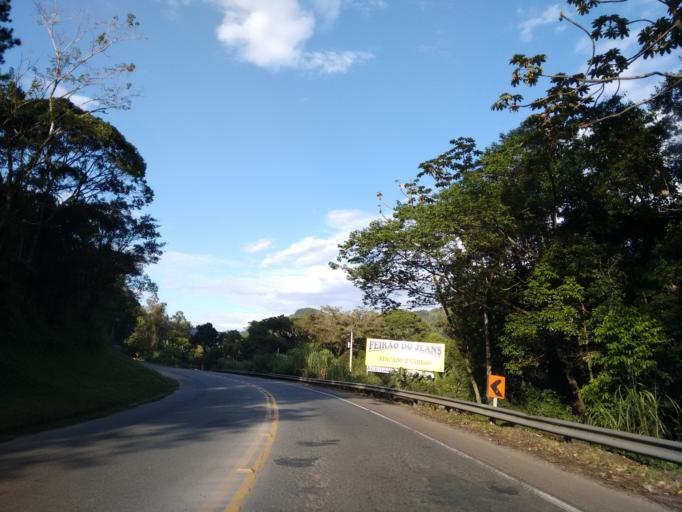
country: BR
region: Santa Catarina
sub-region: Ibirama
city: Ibirama
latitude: -27.0832
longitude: -49.5099
